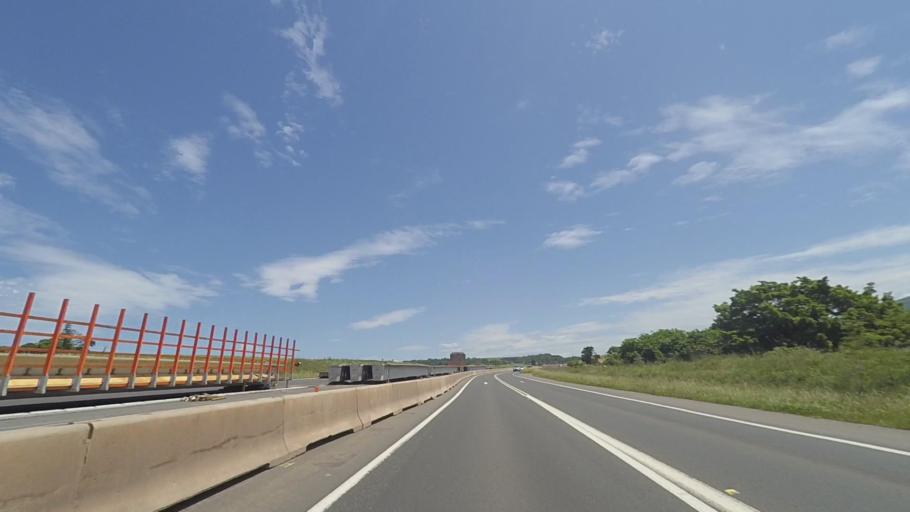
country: AU
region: New South Wales
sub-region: Kiama
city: Gerringong
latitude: -34.7508
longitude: 150.7850
